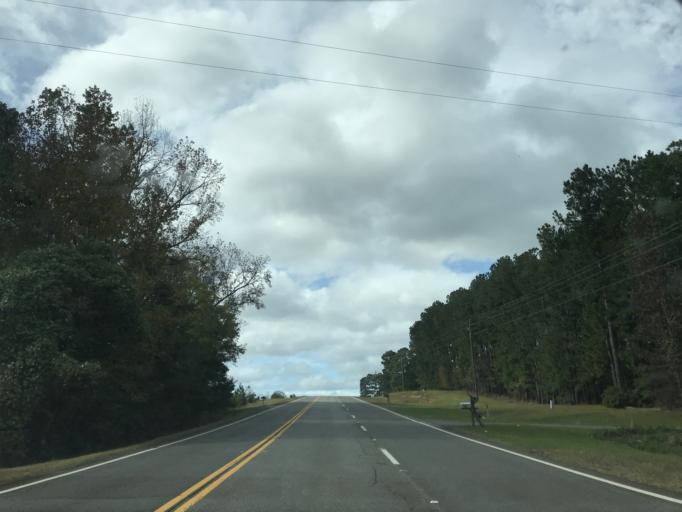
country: US
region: Georgia
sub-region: Jones County
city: Gray
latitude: 32.9706
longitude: -83.4919
